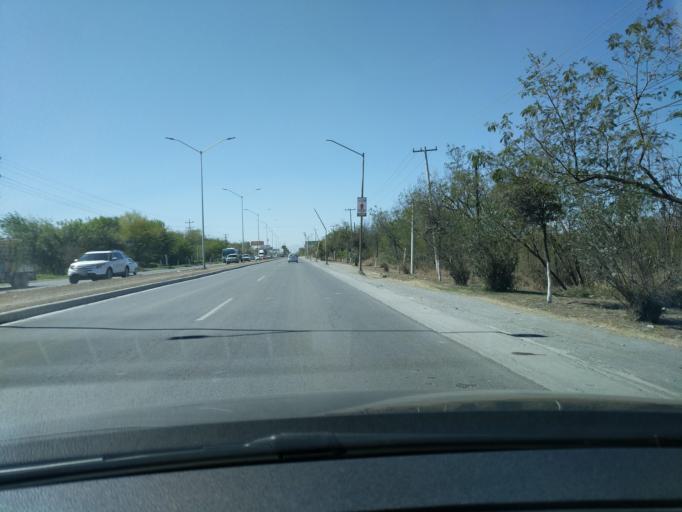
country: MX
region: Nuevo Leon
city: Juarez
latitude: 25.6353
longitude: -100.0815
